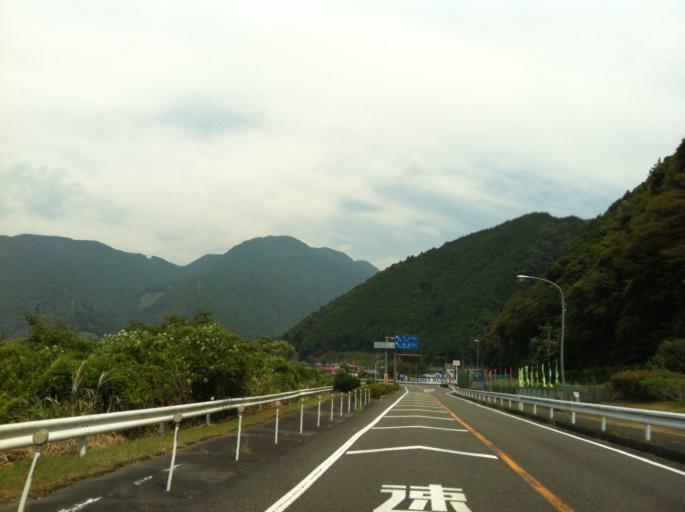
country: JP
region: Shizuoka
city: Shizuoka-shi
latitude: 35.1042
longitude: 138.3665
